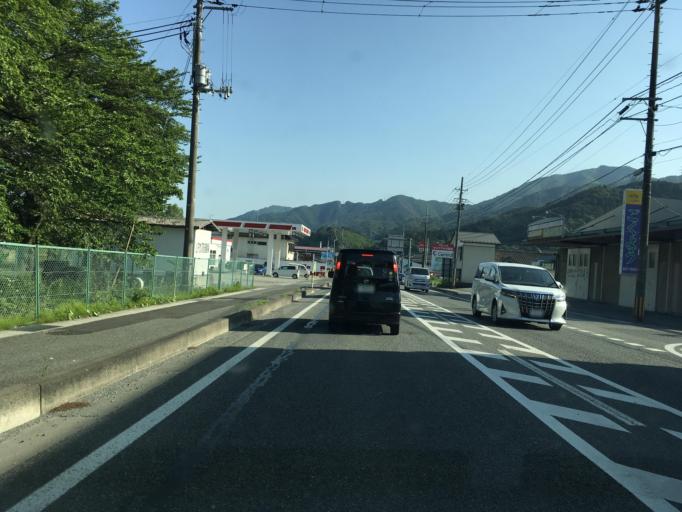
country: JP
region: Iwate
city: Ofunato
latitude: 39.0979
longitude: 141.7076
